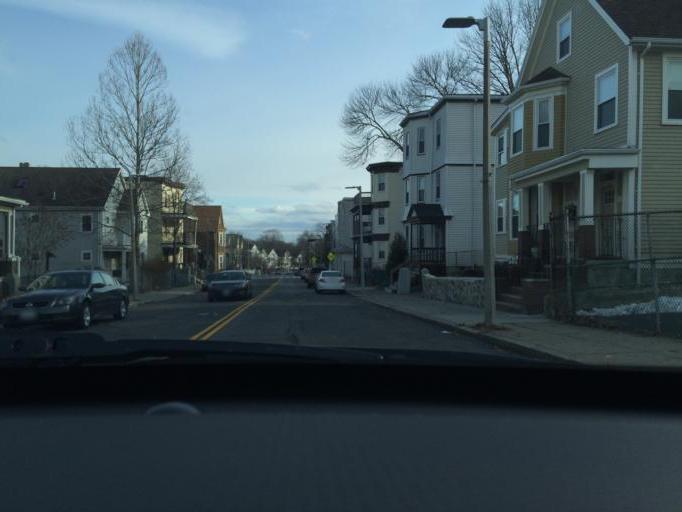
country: US
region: Massachusetts
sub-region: Suffolk County
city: Jamaica Plain
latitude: 42.3015
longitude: -71.0849
